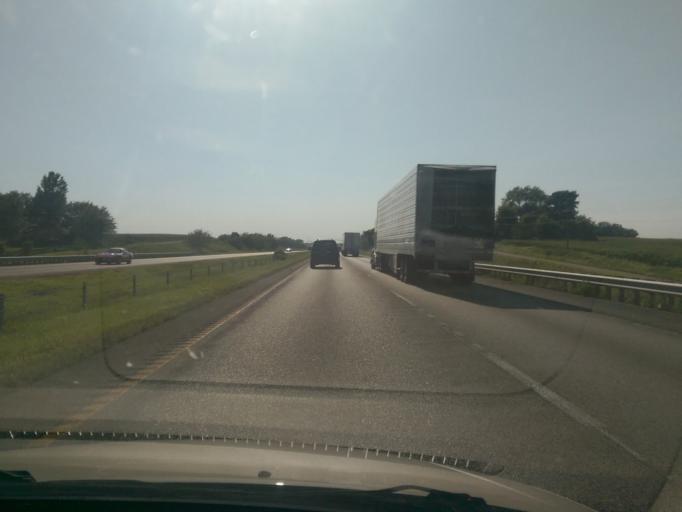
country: US
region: Missouri
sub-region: Lafayette County
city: Higginsville
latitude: 39.0031
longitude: -93.8214
